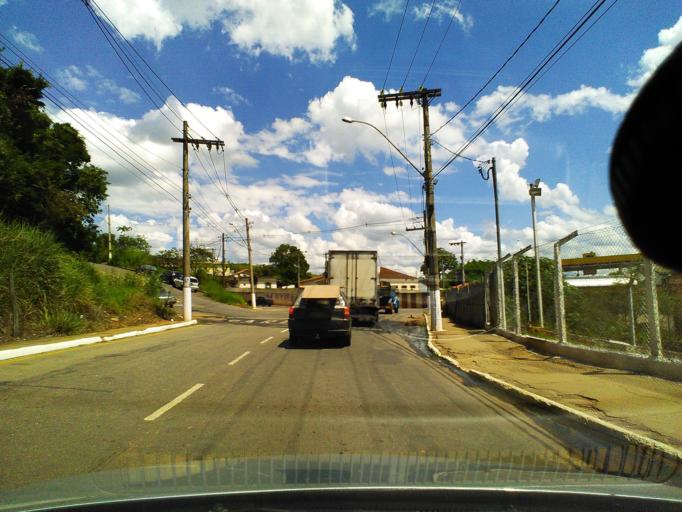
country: BR
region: Minas Gerais
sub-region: Tres Coracoes
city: Tres Coracoes
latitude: -21.7090
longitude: -45.2631
